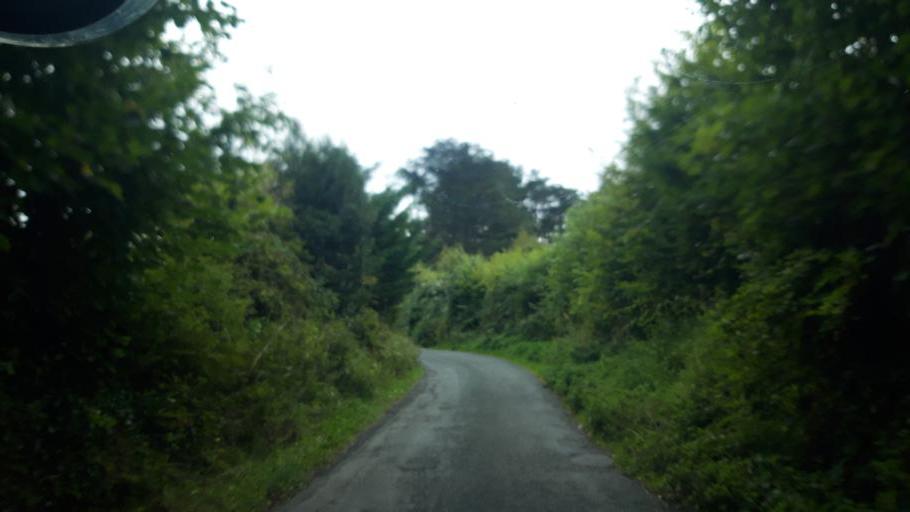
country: IE
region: Leinster
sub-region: Wicklow
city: Enniskerry
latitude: 53.1787
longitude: -6.2045
